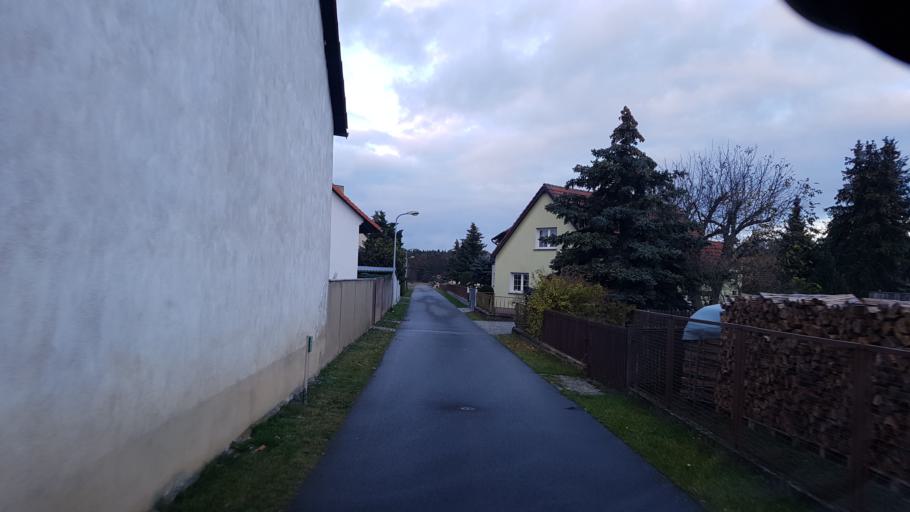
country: DE
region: Brandenburg
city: Tettau
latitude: 51.4182
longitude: 13.7697
